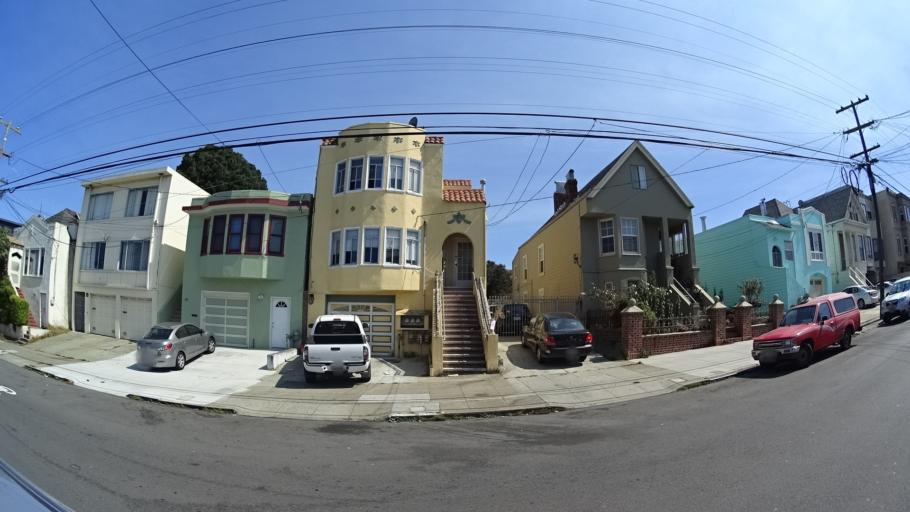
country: US
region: California
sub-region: San Mateo County
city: Daly City
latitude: 37.7232
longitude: -122.4562
